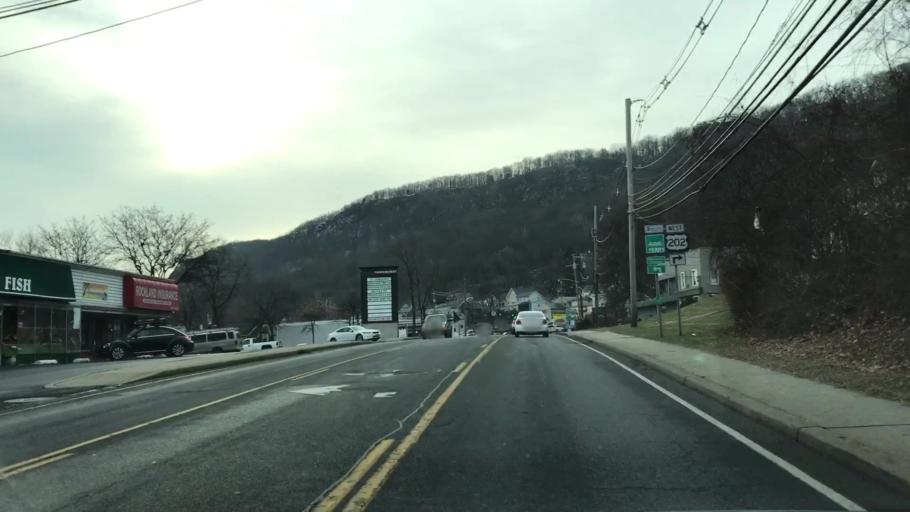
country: US
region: New York
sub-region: Rockland County
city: West Haverstraw
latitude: 41.2004
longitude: -73.9833
